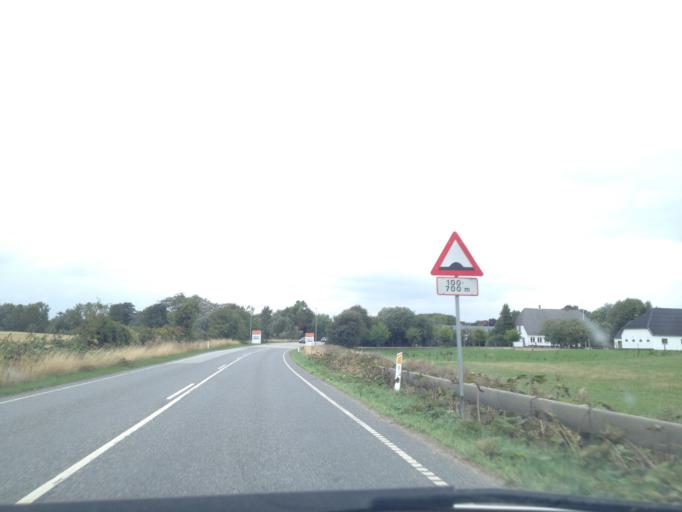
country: DK
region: South Denmark
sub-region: Haderslev Kommune
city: Starup
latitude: 55.2957
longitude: 9.5616
